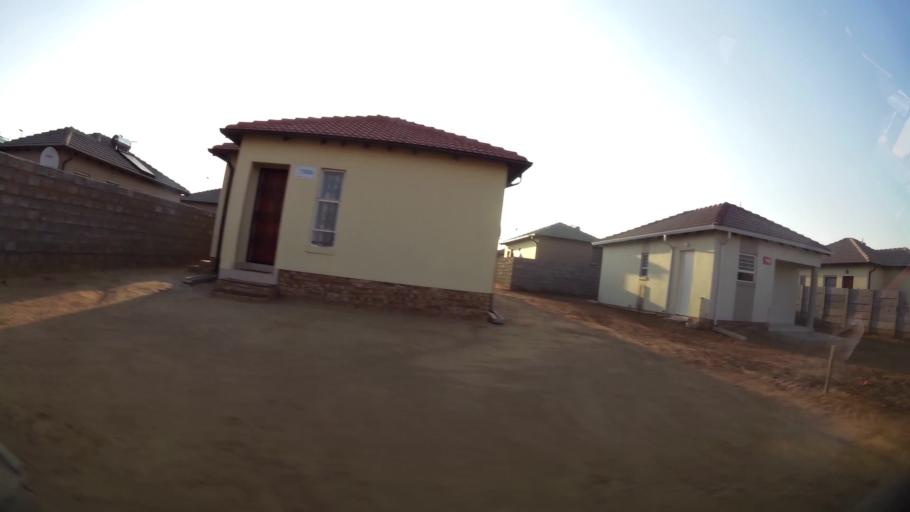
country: ZA
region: Gauteng
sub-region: Ekurhuleni Metropolitan Municipality
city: Benoni
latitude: -26.1431
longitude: 28.3824
